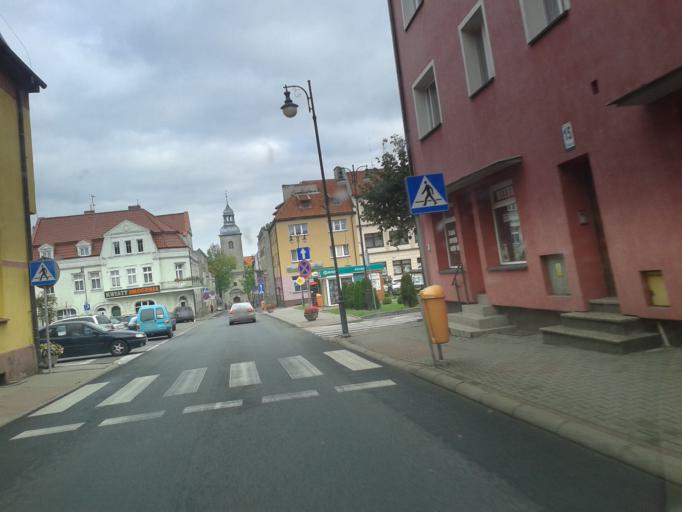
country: PL
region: Kujawsko-Pomorskie
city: Kamien Krajenski
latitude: 53.5333
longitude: 17.5193
